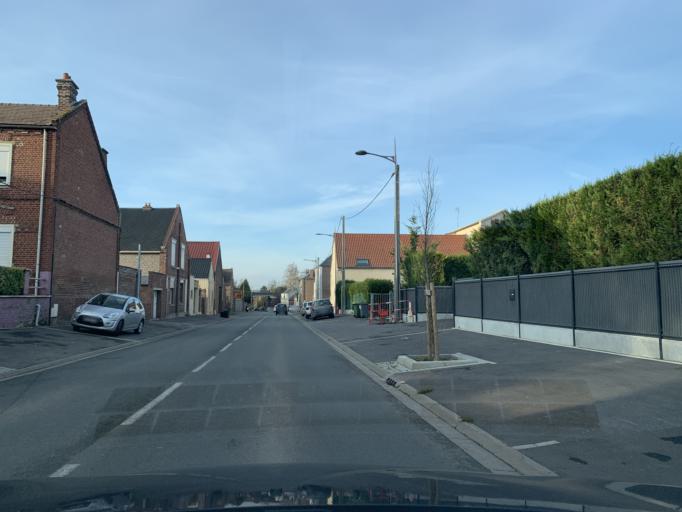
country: FR
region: Nord-Pas-de-Calais
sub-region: Departement du Nord
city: Cambrai
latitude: 50.1595
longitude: 3.2520
